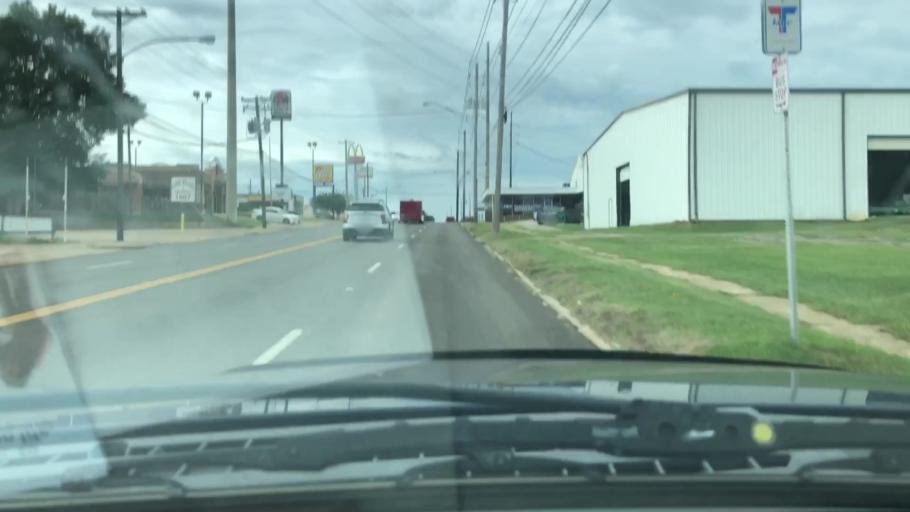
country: US
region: Texas
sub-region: Bowie County
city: Texarkana
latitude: 33.4351
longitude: -94.0592
